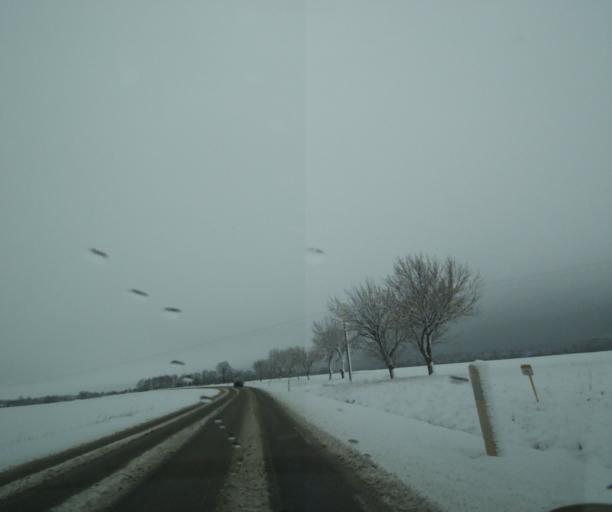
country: FR
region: Champagne-Ardenne
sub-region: Departement de la Haute-Marne
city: Wassy
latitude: 48.5365
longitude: 4.9251
